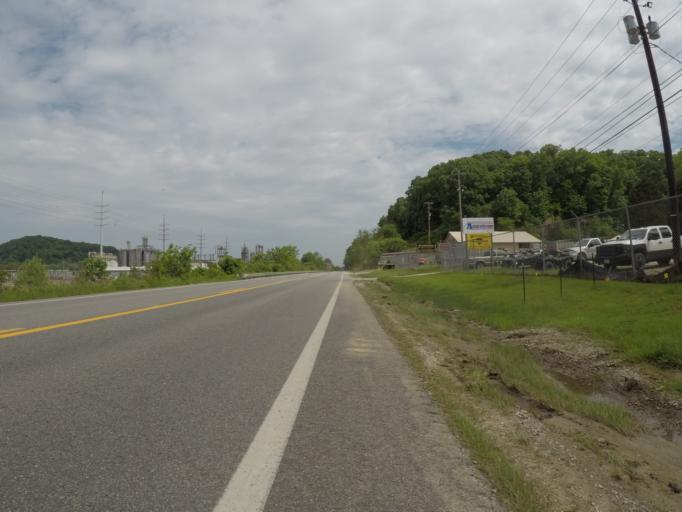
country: US
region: West Virginia
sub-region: Wayne County
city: Kenova
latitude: 38.3514
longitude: -82.5933
